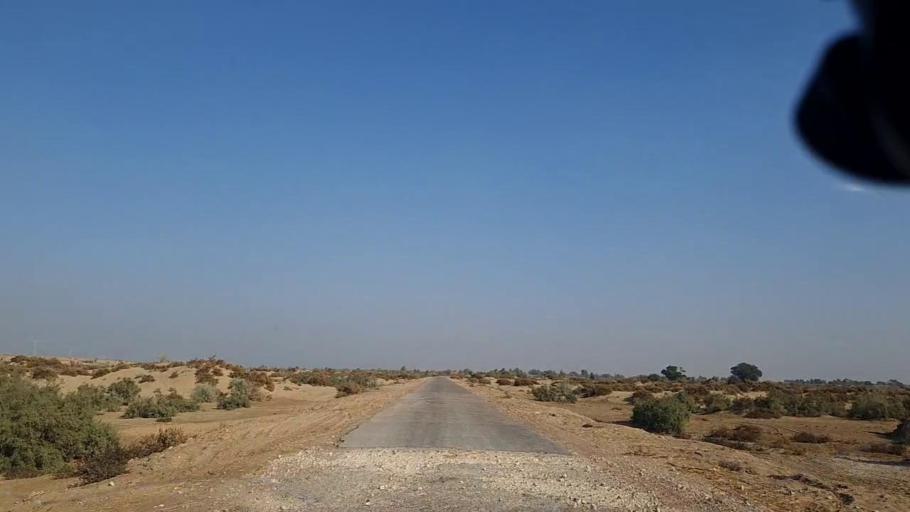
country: PK
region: Sindh
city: Khanpur
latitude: 27.6863
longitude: 69.4697
